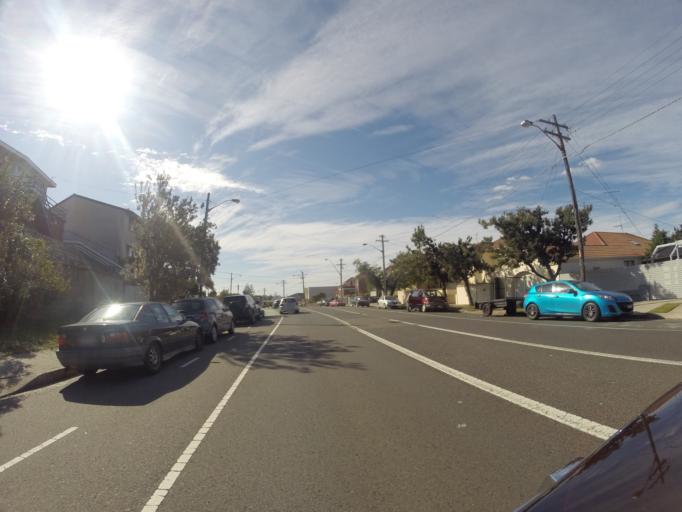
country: AU
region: New South Wales
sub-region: Randwick
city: South Coogee
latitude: -33.9384
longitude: 151.2573
